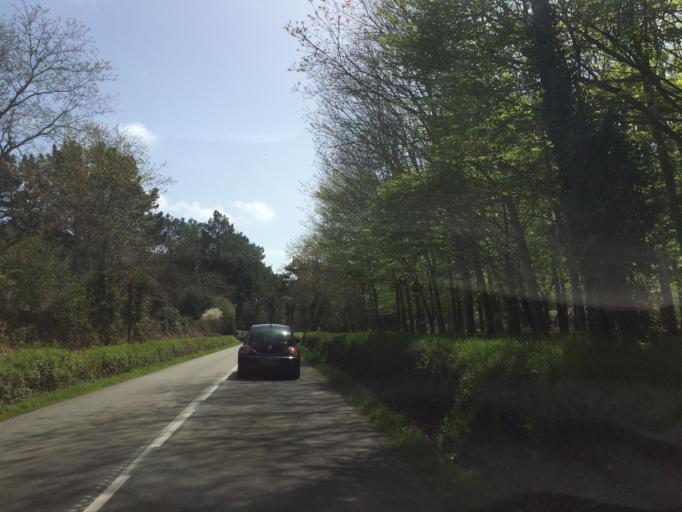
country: FR
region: Brittany
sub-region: Departement du Morbihan
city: Ploemel
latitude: 47.6295
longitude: -3.0495
